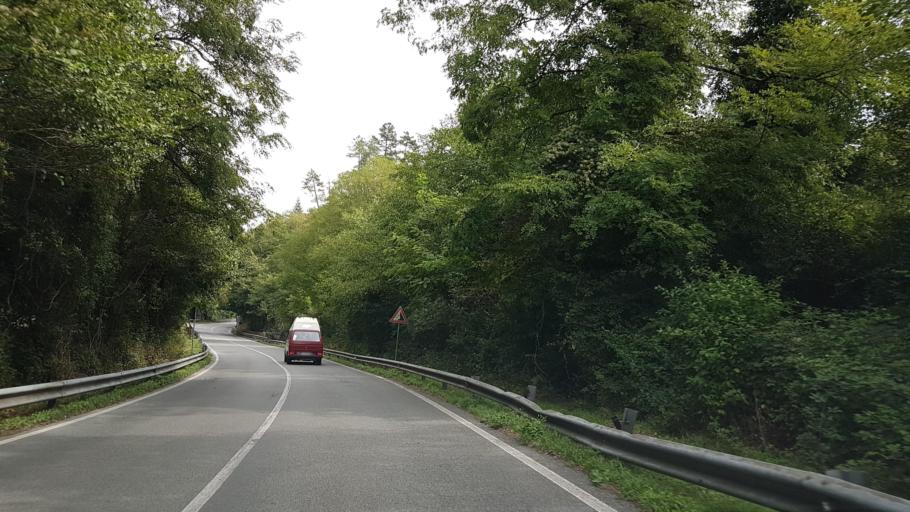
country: IT
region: Liguria
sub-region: Provincia di La Spezia
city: Carrodano
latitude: 44.2284
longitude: 9.6356
